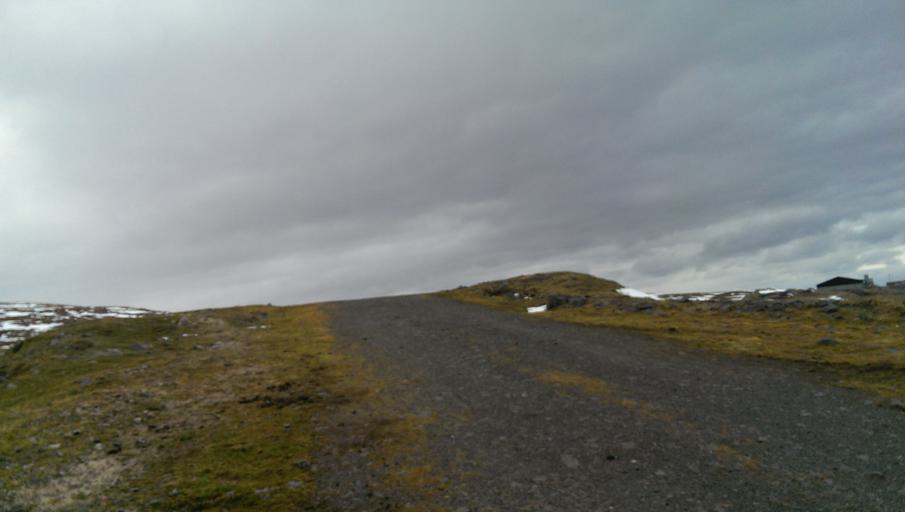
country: FO
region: Streymoy
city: Hoyvik
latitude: 62.0341
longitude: -6.8054
